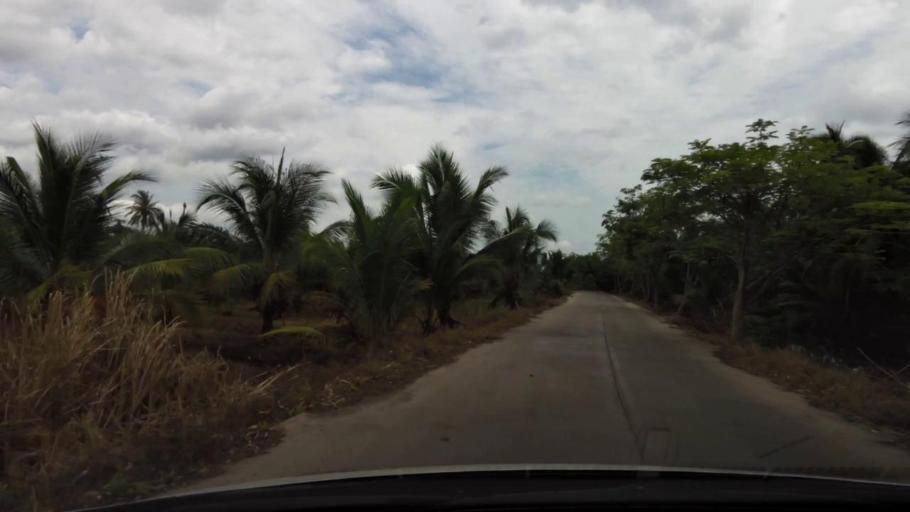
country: TH
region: Samut Sakhon
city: Ban Phaeo
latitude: 13.5648
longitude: 100.0387
